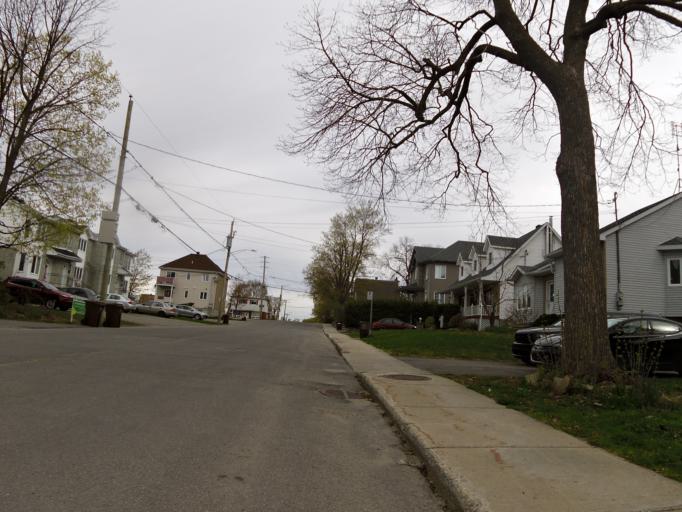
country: CA
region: Quebec
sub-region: Laurentides
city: Deux-Montagnes
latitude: 45.5363
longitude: -73.8850
